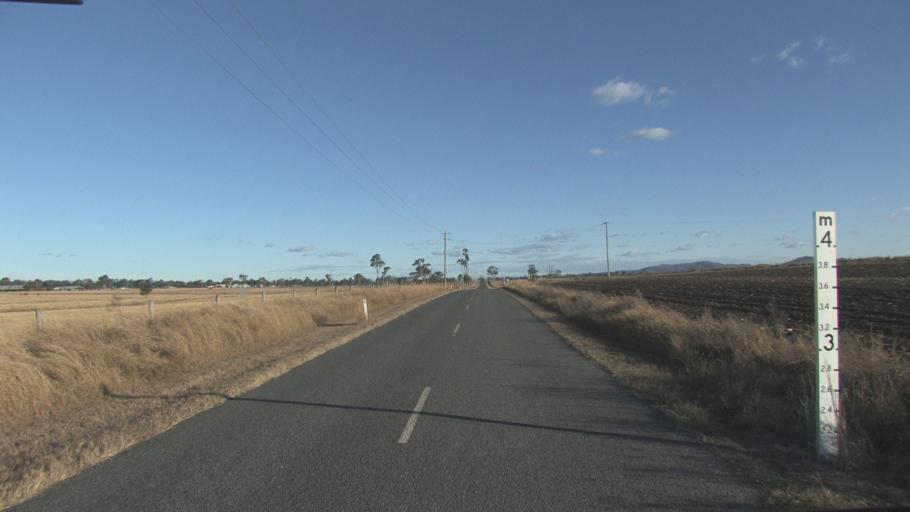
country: AU
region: Queensland
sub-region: Logan
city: Cedar Vale
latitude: -27.8633
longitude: 152.9585
